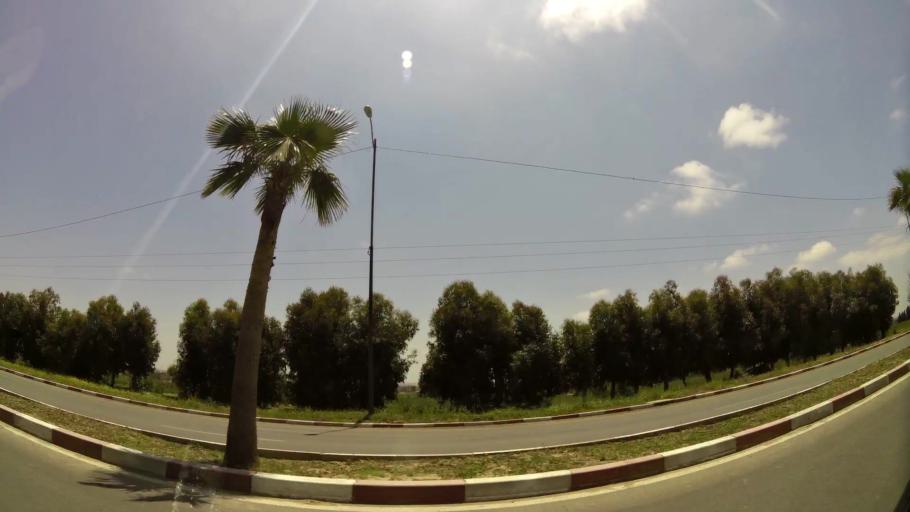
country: MA
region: Fes-Boulemane
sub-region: Fes
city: Fes
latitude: 34.0443
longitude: -5.0582
